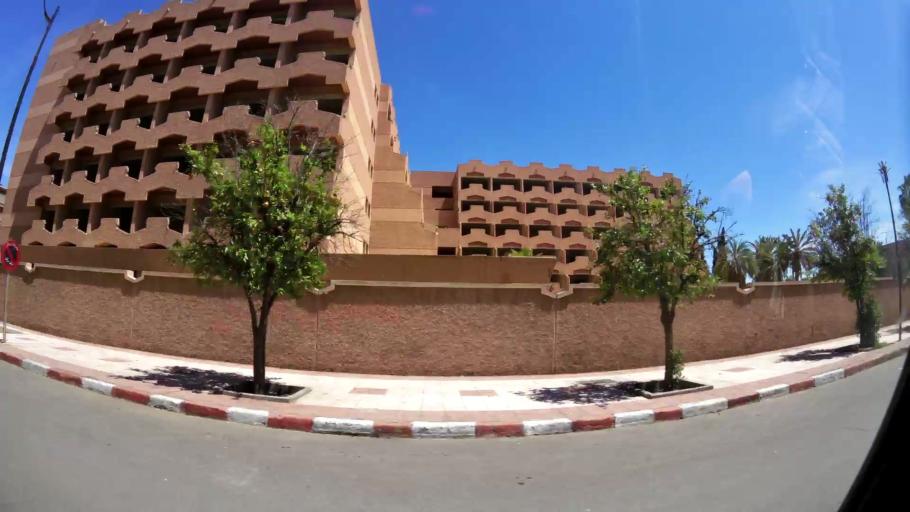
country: MA
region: Marrakech-Tensift-Al Haouz
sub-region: Marrakech
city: Marrakesh
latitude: 31.6225
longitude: -8.0039
